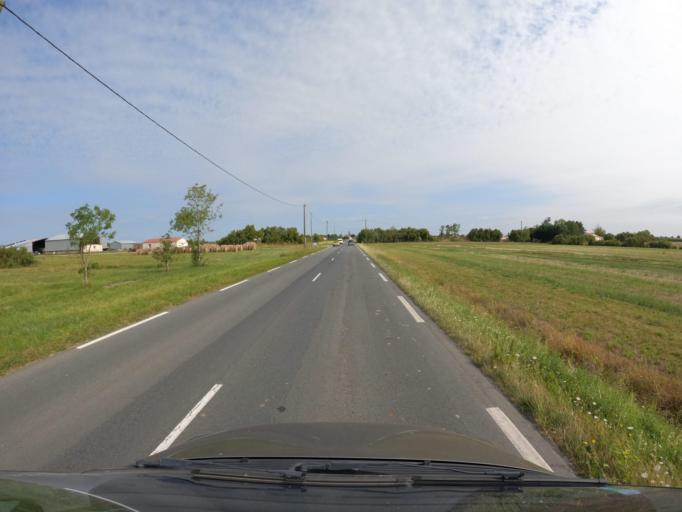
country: FR
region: Pays de la Loire
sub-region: Departement de la Vendee
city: Triaize
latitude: 46.3853
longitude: -1.2021
